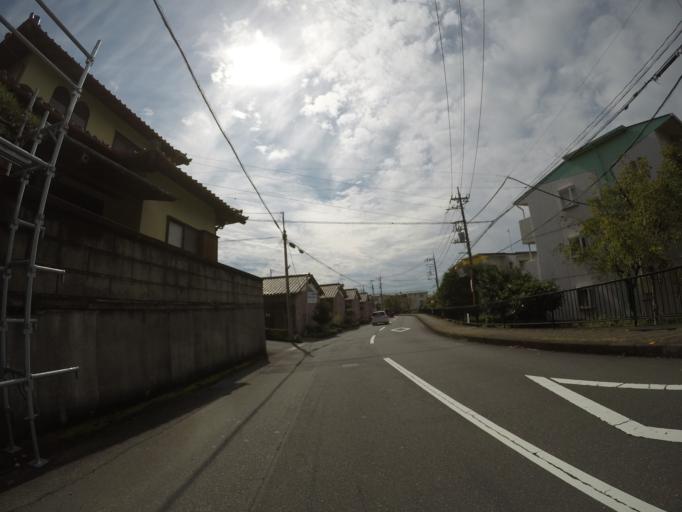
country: JP
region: Shizuoka
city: Fuji
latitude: 35.1847
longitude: 138.6915
